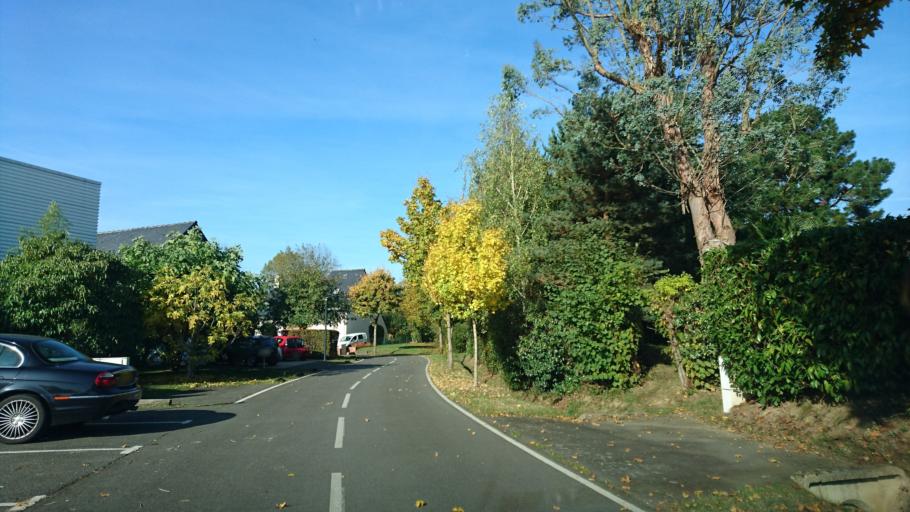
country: FR
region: Brittany
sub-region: Departement d'Ille-et-Vilaine
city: Chavagne
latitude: 48.0396
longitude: -1.7657
